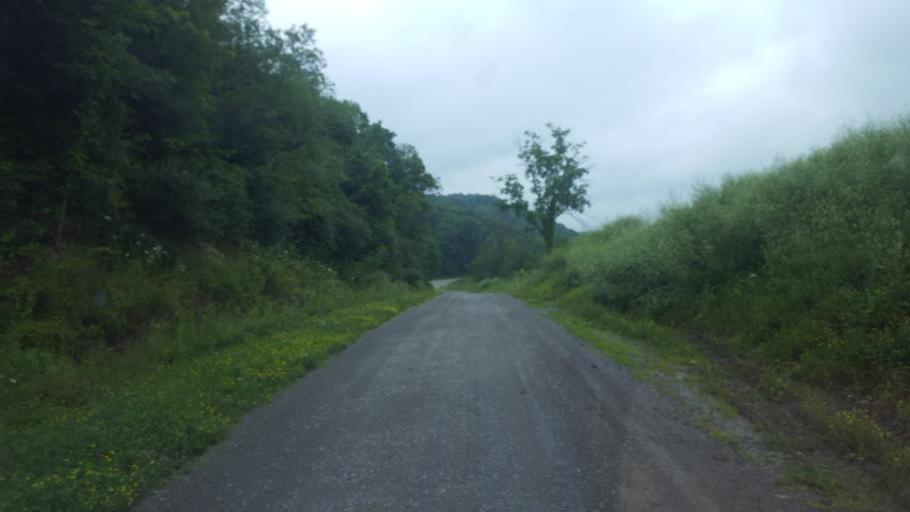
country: US
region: Ohio
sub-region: Columbiana County
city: Salineville
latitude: 40.5620
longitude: -80.8284
